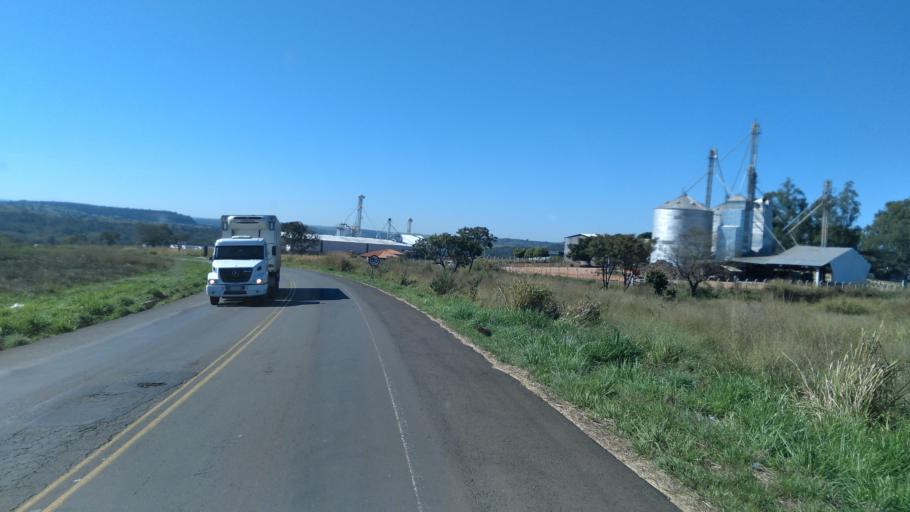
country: BR
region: Goias
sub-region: Mineiros
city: Mineiros
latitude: -17.5797
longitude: -52.5158
